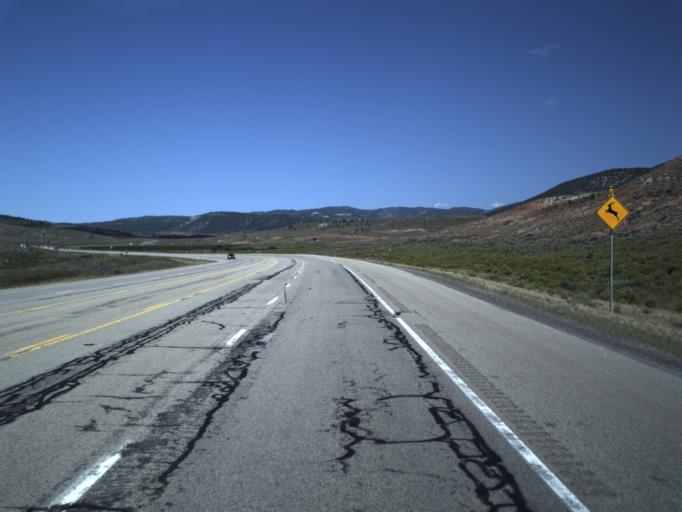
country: US
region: Utah
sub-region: Carbon County
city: Helper
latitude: 39.8726
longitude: -111.0337
